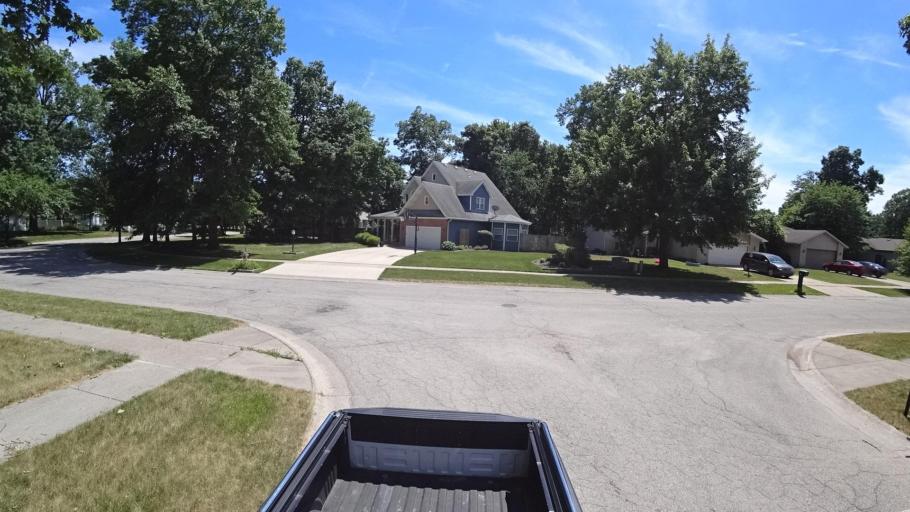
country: US
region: Indiana
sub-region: Porter County
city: Porter
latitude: 41.6034
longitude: -87.0967
